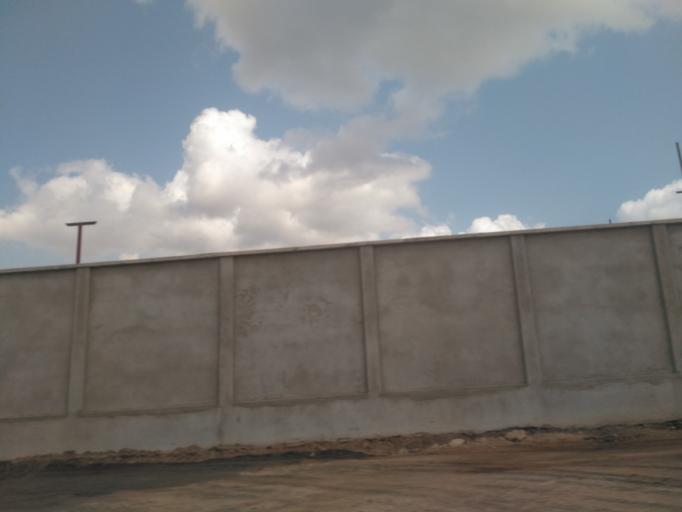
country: TZ
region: Dar es Salaam
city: Dar es Salaam
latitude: -6.8462
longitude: 39.3169
